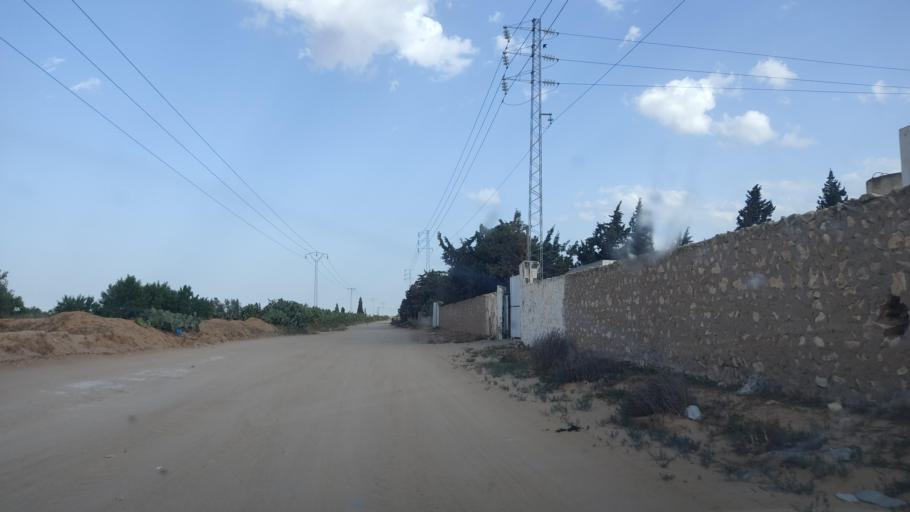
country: TN
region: Safaqis
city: Sfax
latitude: 34.8591
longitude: 10.6020
